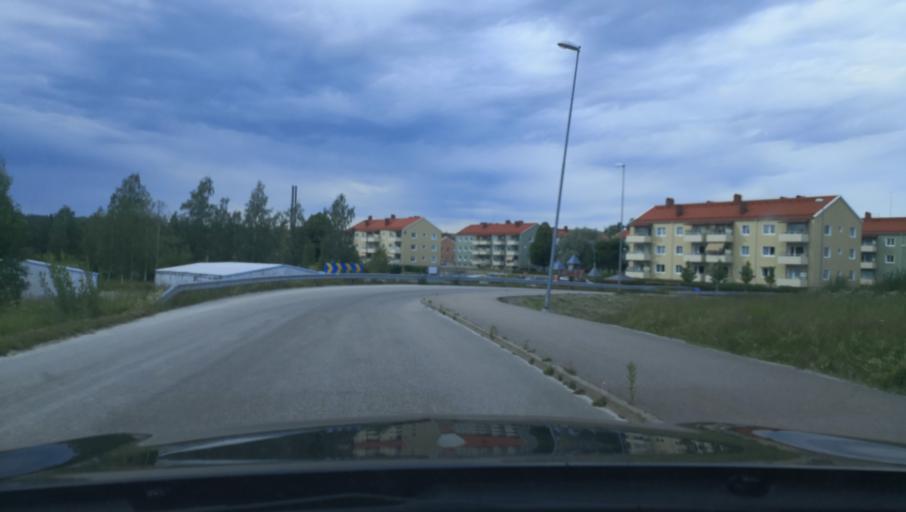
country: SE
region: Vaestmanland
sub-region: Fagersta Kommun
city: Fagersta
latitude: 59.9851
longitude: 15.8246
